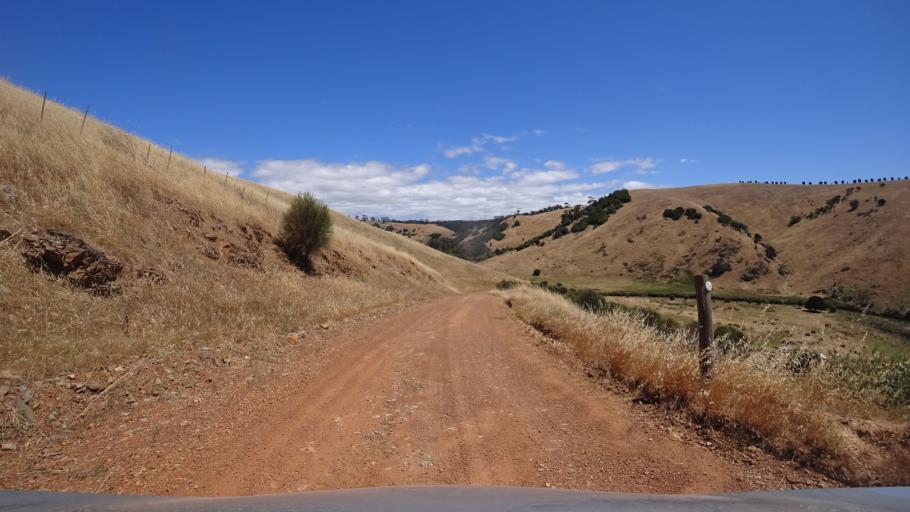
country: AU
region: South Australia
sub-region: Kangaroo Island
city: Kingscote
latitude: -35.6778
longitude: 136.9729
